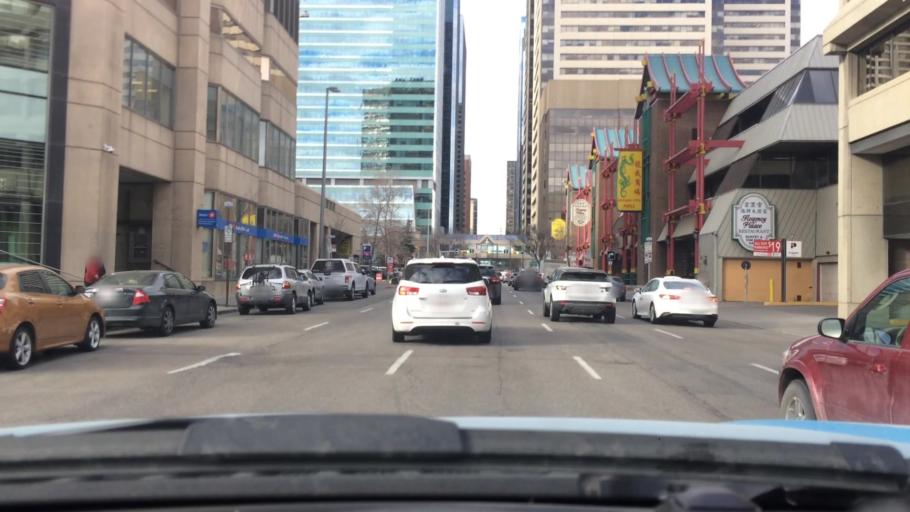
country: CA
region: Alberta
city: Calgary
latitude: 51.0493
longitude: -114.0605
